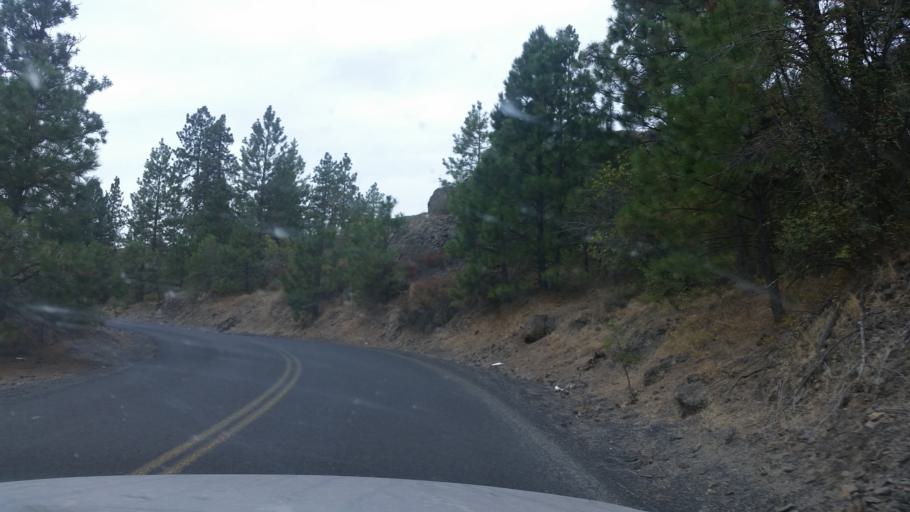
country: US
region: Washington
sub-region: Spokane County
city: Spokane
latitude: 47.6552
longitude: -117.4834
